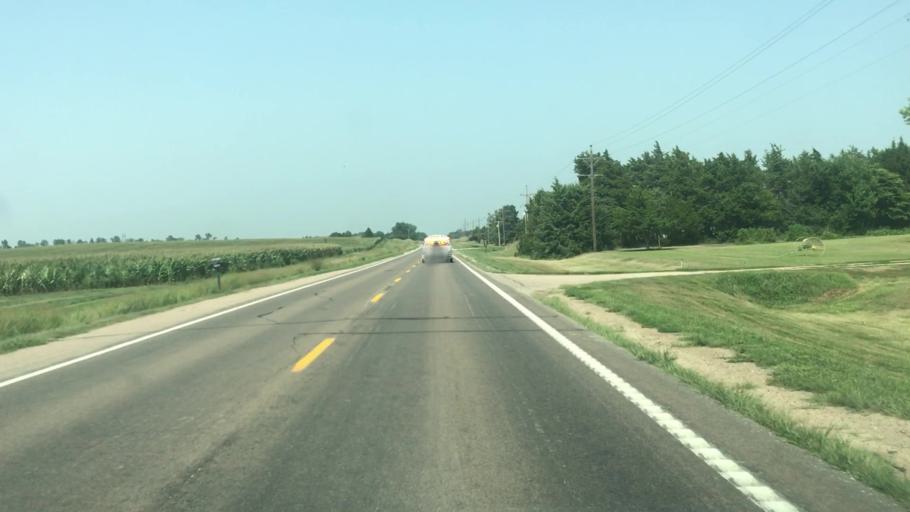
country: US
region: Nebraska
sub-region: Hall County
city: Wood River
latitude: 41.0196
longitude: -98.6070
